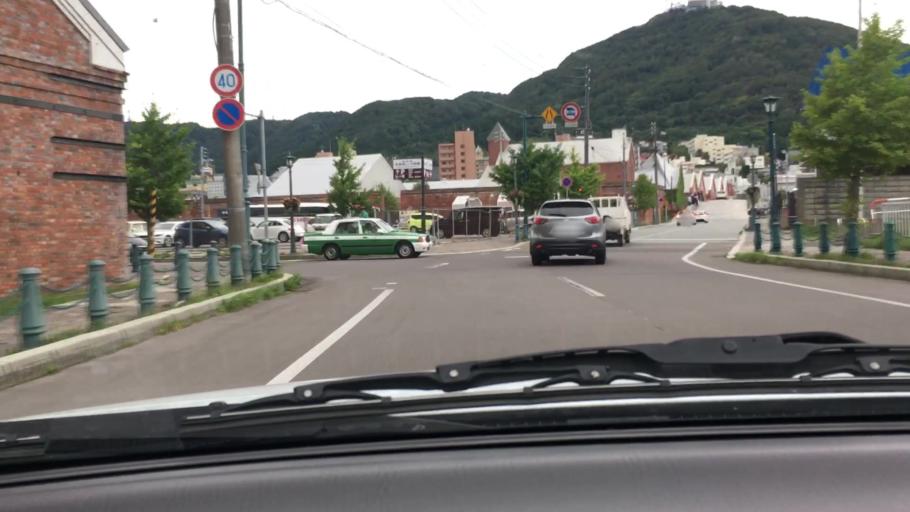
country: JP
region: Hokkaido
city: Hakodate
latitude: 41.7680
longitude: 140.7186
